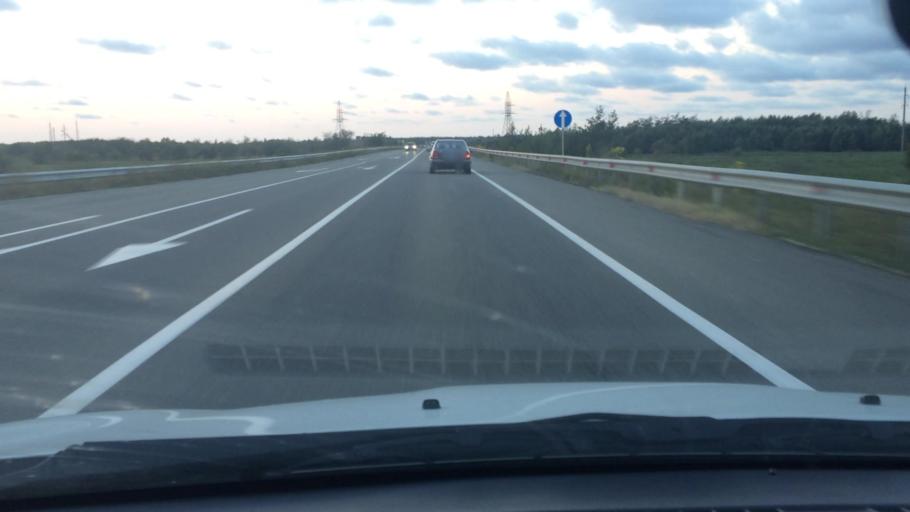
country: GE
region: Ajaria
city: Ochkhamuri
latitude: 41.9022
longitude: 41.7930
